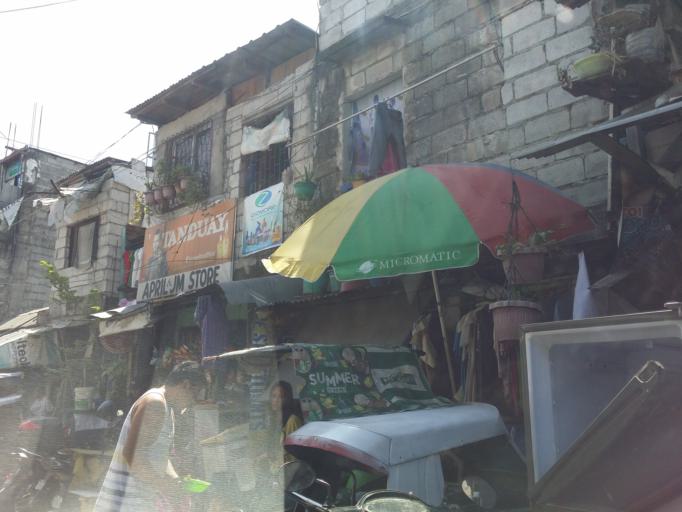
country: PH
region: Metro Manila
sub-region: Mandaluyong
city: Mandaluyong City
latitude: 14.5830
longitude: 121.0350
